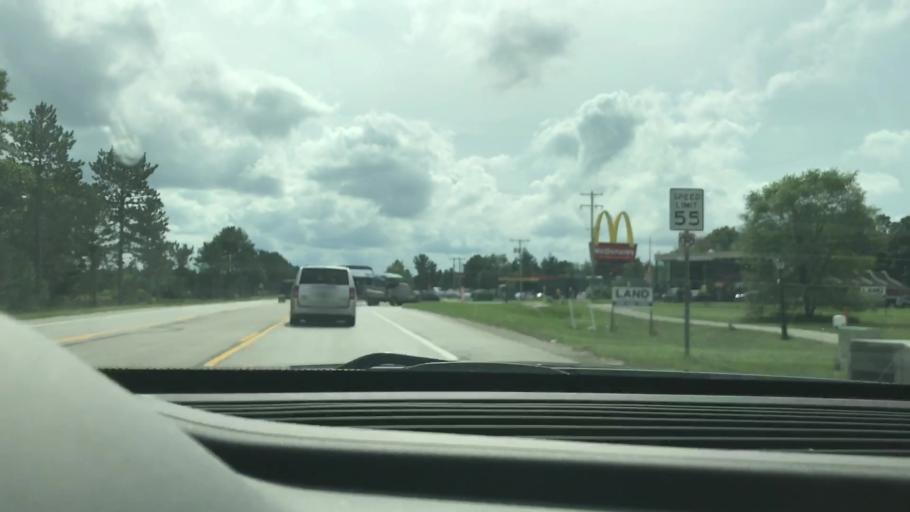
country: US
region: Michigan
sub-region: Kalkaska County
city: Kalkaska
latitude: 44.7261
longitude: -85.1826
